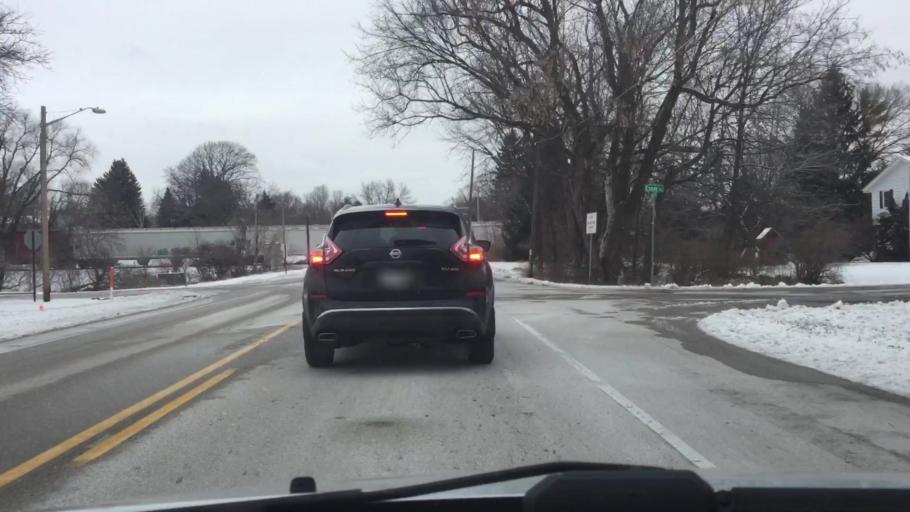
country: US
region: Wisconsin
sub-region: Waukesha County
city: Brookfield
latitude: 43.0660
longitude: -88.1061
